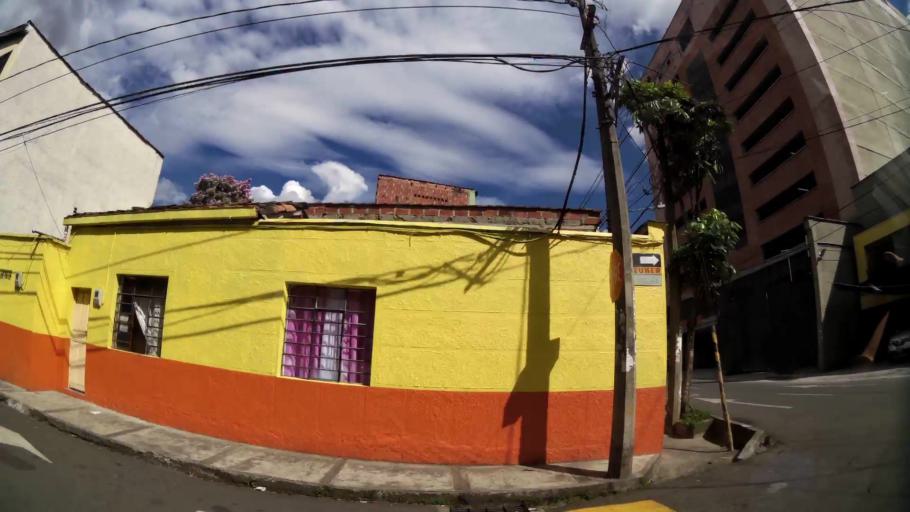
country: CO
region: Antioquia
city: Sabaneta
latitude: 6.1553
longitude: -75.6116
